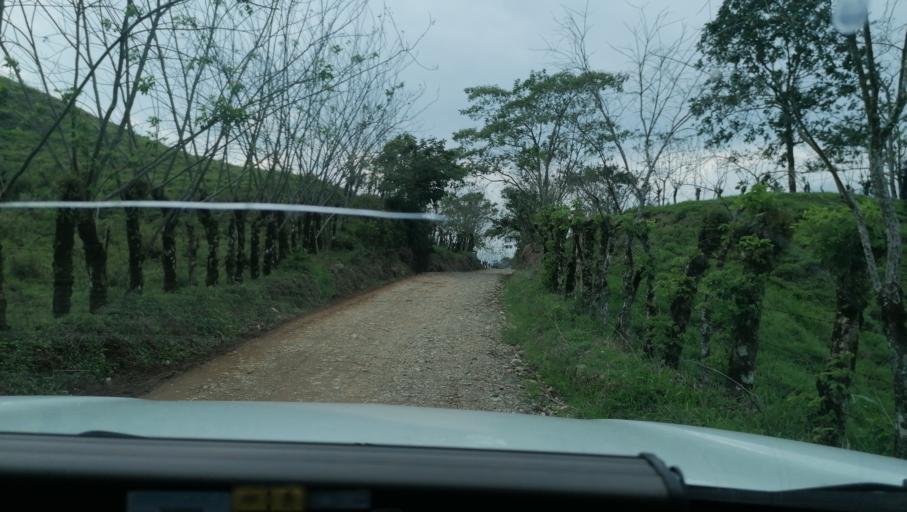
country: MX
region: Chiapas
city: Ixtacomitan
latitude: 17.3392
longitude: -93.1163
